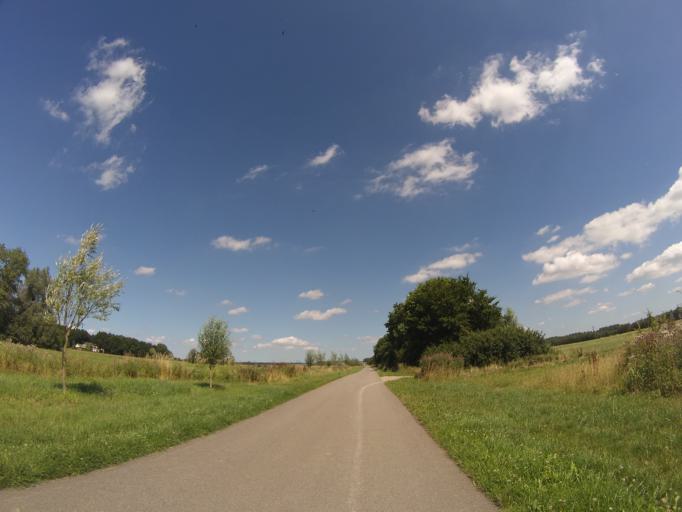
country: NL
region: Utrecht
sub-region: Stichtse Vecht
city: Spechtenkamp
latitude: 52.1255
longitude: 5.0005
